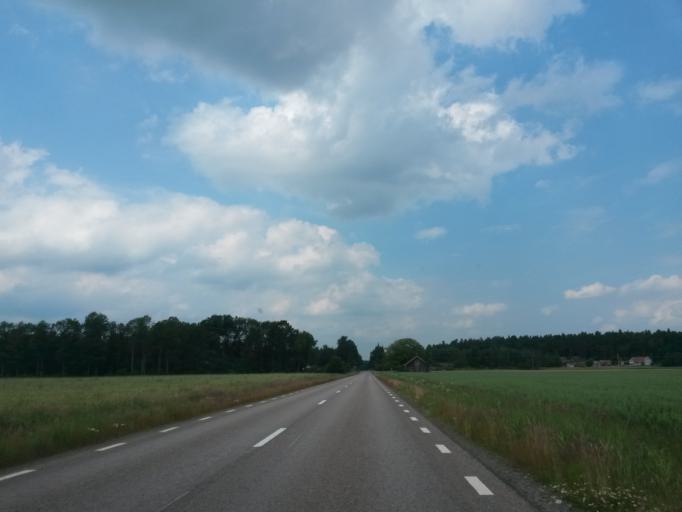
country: SE
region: Vaestra Goetaland
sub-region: Essunga Kommun
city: Nossebro
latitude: 58.2528
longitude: 12.6957
